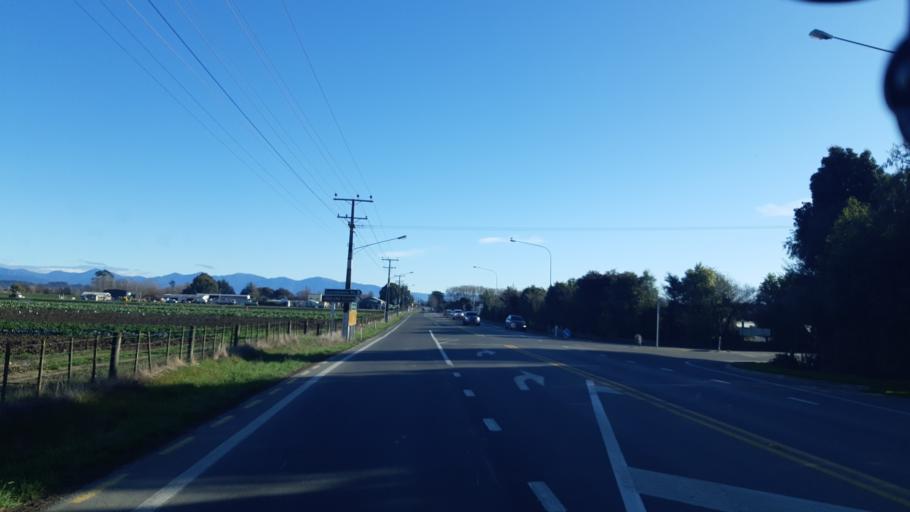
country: NZ
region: Tasman
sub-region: Tasman District
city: Richmond
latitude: -41.3168
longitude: 173.1362
